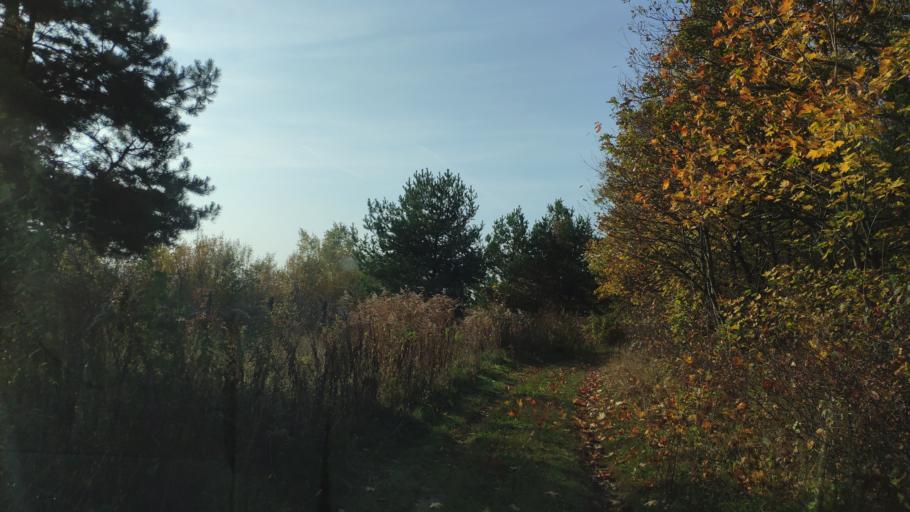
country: SK
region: Kosicky
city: Kosice
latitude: 48.7453
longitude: 21.2202
